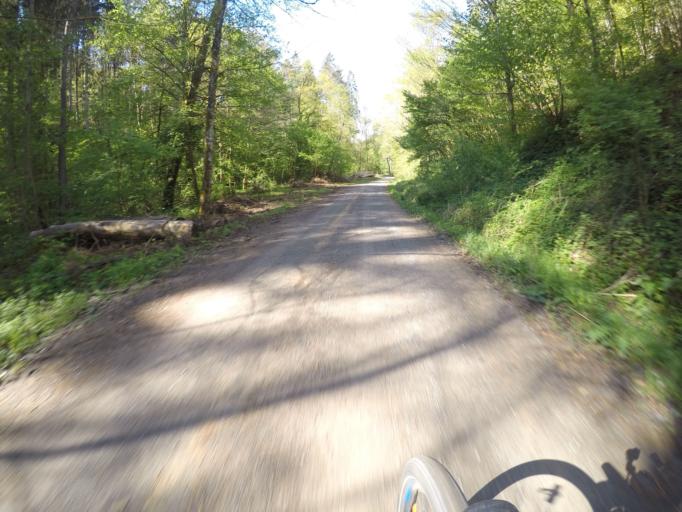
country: DE
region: Baden-Wuerttemberg
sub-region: Tuebingen Region
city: Tuebingen
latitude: 48.5557
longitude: 9.0839
